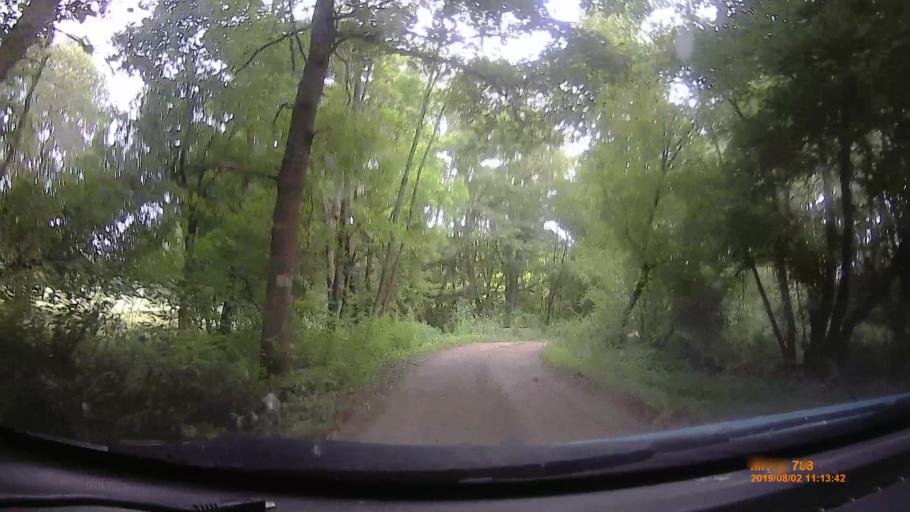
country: HU
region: Baranya
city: Buekkoesd
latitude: 46.1131
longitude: 17.9358
